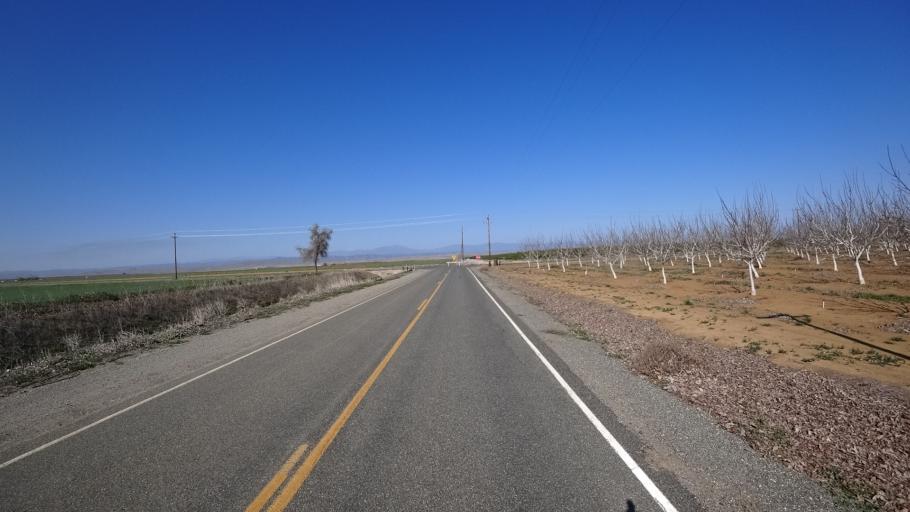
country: US
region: California
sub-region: Glenn County
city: Willows
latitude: 39.4948
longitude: -122.2479
